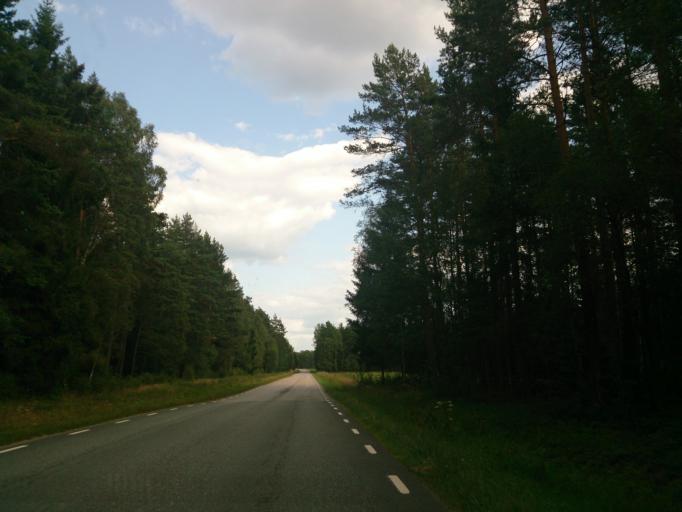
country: SE
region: Joenkoeping
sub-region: Gislaveds Kommun
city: Reftele
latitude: 57.1372
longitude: 13.6378
